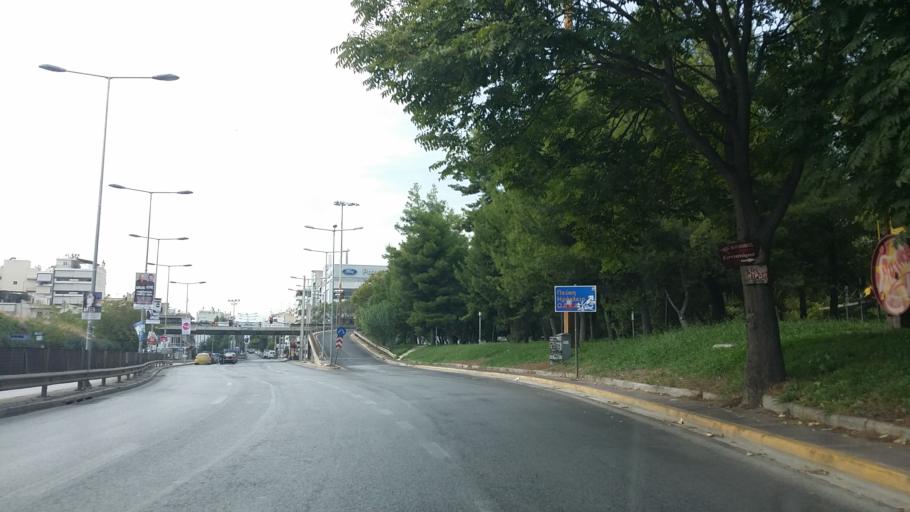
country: GR
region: Attica
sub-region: Nomarchia Athinas
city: Filothei
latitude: 38.0338
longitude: 23.7730
